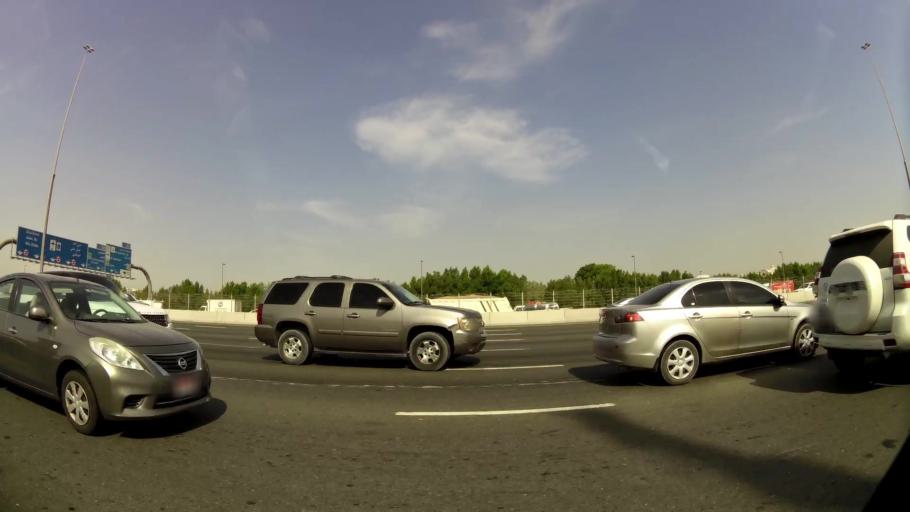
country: AE
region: Ash Shariqah
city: Sharjah
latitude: 25.2467
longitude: 55.4053
